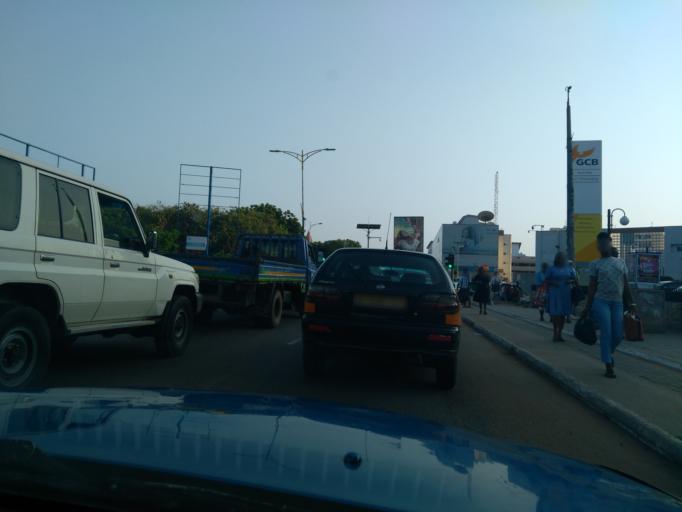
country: GH
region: Greater Accra
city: Accra
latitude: 5.5433
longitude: -0.2052
